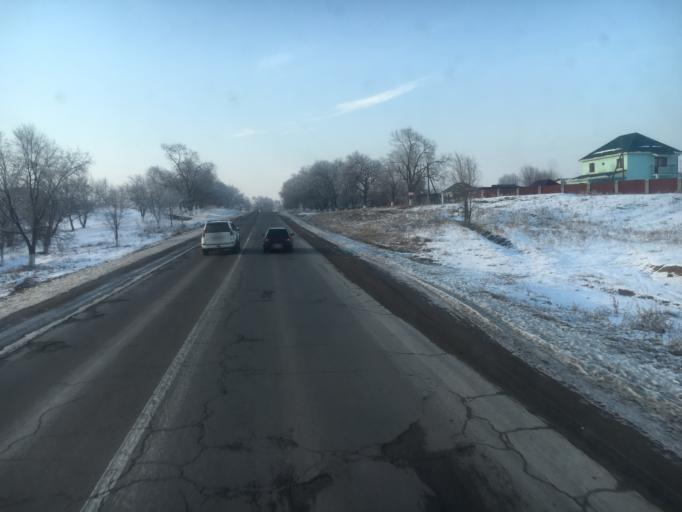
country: KZ
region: Almaty Oblysy
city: Burunday
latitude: 43.3056
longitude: 76.6698
